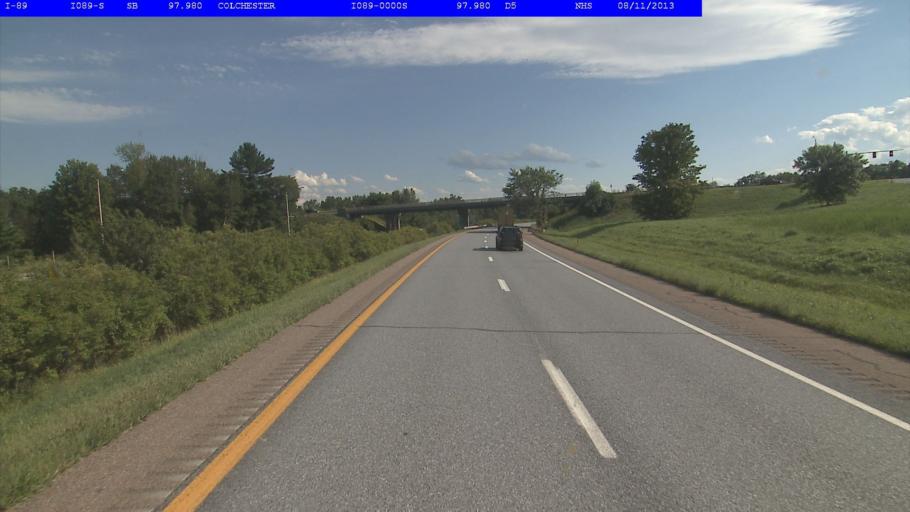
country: US
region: Vermont
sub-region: Chittenden County
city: Colchester
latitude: 44.5914
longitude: -73.1705
